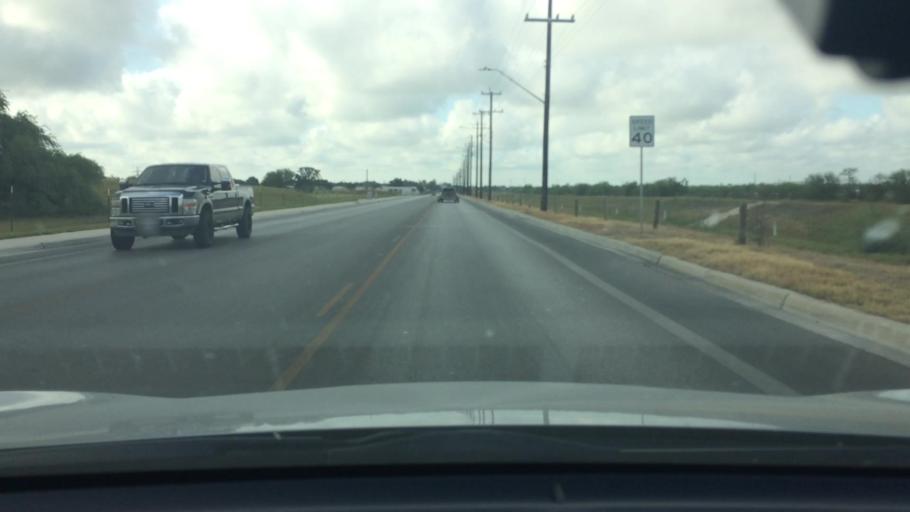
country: US
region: Texas
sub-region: Bexar County
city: China Grove
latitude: 29.3458
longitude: -98.4274
